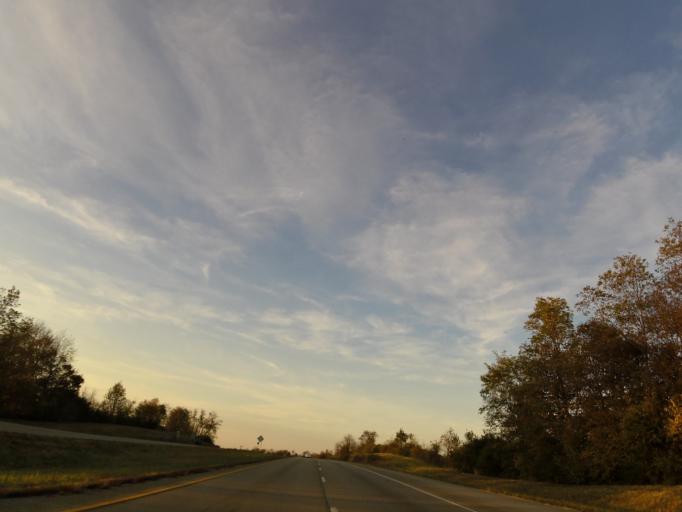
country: US
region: Kentucky
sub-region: Jessamine County
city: Nicholasville
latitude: 37.8529
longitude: -84.5873
